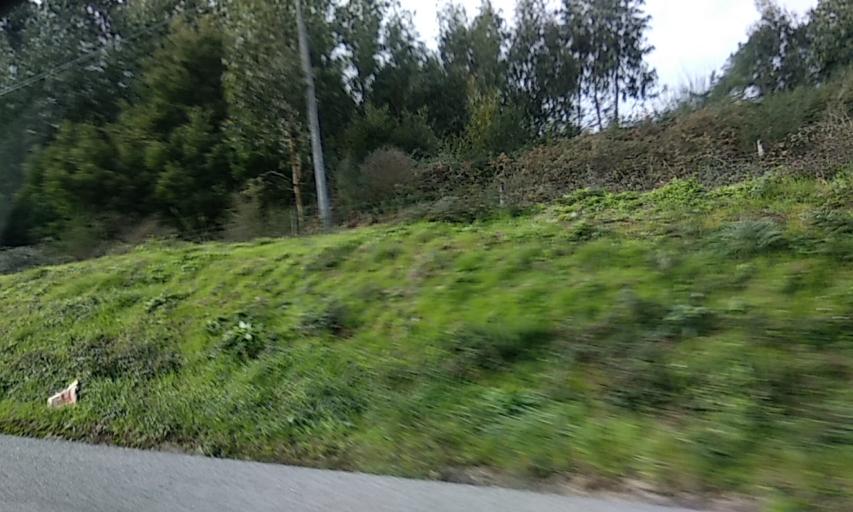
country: PT
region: Braga
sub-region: Vila Nova de Famalicao
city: Vila Nova de Famalicao
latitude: 41.4217
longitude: -8.4941
